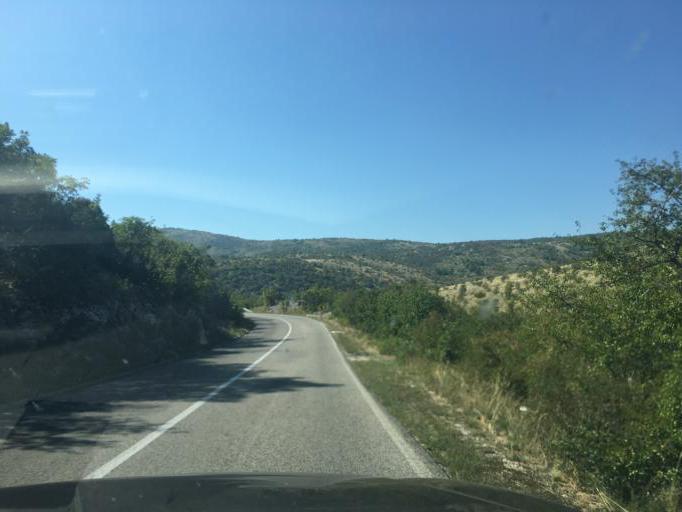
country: HR
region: Splitsko-Dalmatinska
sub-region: Grad Trogir
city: Trogir
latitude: 43.5672
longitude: 16.2464
